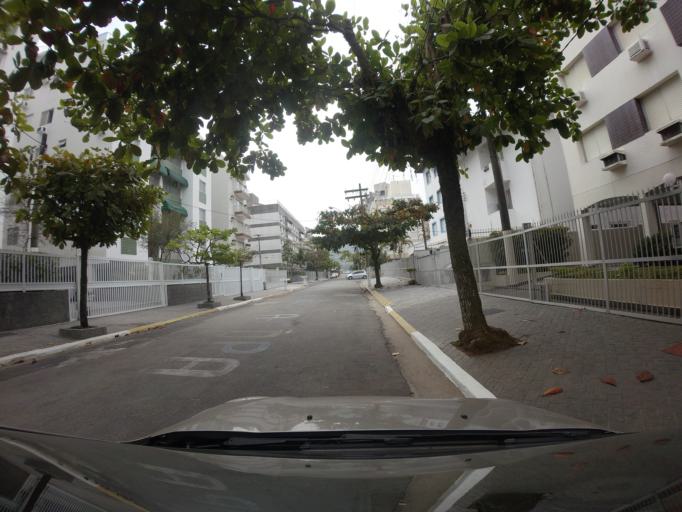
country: BR
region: Sao Paulo
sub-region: Guaruja
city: Guaruja
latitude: -23.9846
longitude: -46.2330
